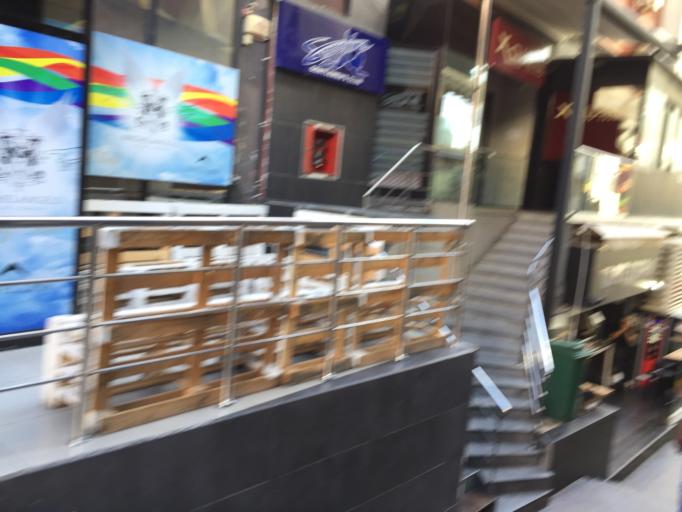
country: MT
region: Saint Julian
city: San Giljan
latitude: 35.9242
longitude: 14.4888
